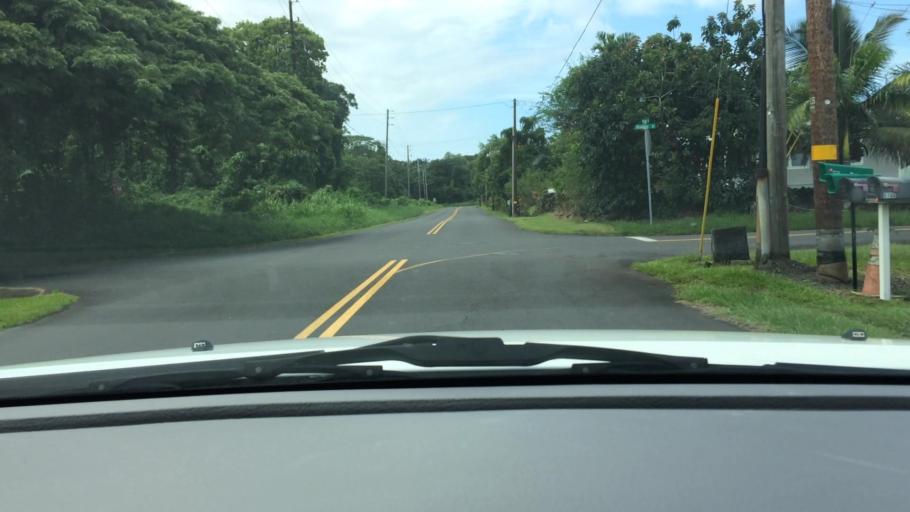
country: US
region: Hawaii
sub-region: Hawaii County
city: Hilo
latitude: 19.7139
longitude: -155.0714
